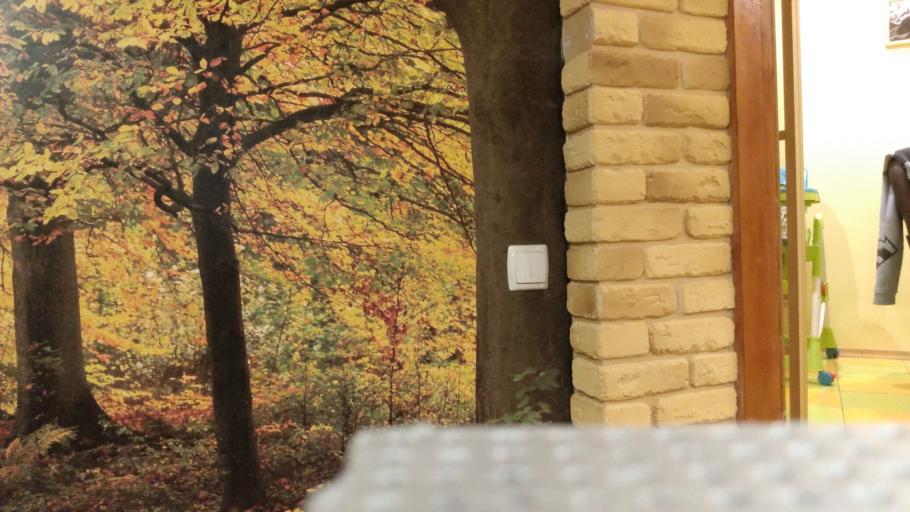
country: RU
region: Vologda
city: Babayevo
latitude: 59.3718
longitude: 35.9940
